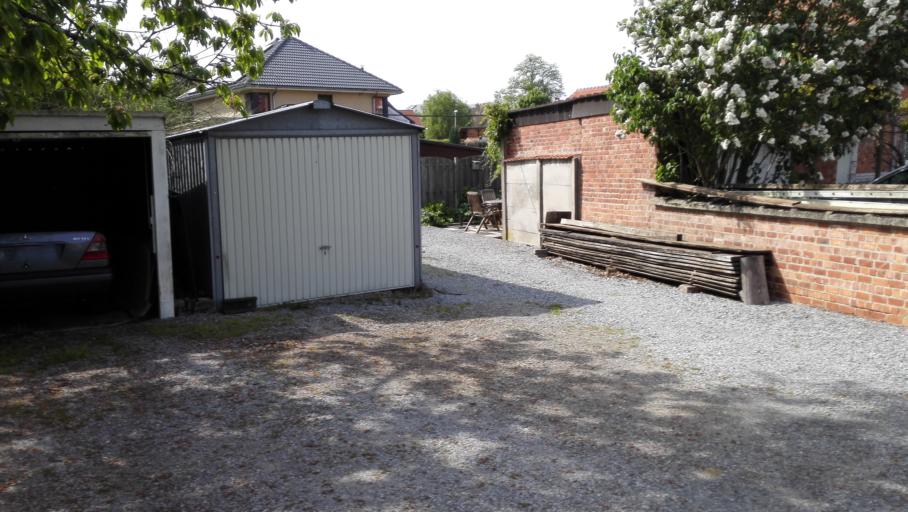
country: BE
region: Flanders
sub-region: Provincie Vlaams-Brabant
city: Holsbeek
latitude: 50.8850
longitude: 4.7642
